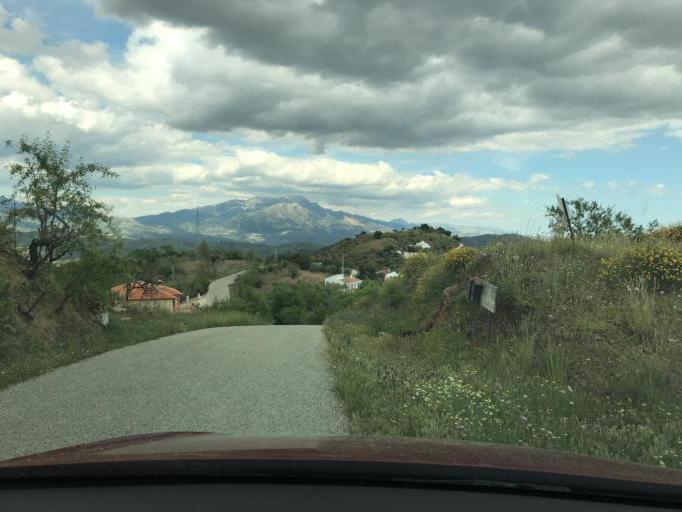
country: ES
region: Andalusia
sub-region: Provincia de Malaga
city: Comares
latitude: 36.8698
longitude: -4.2743
